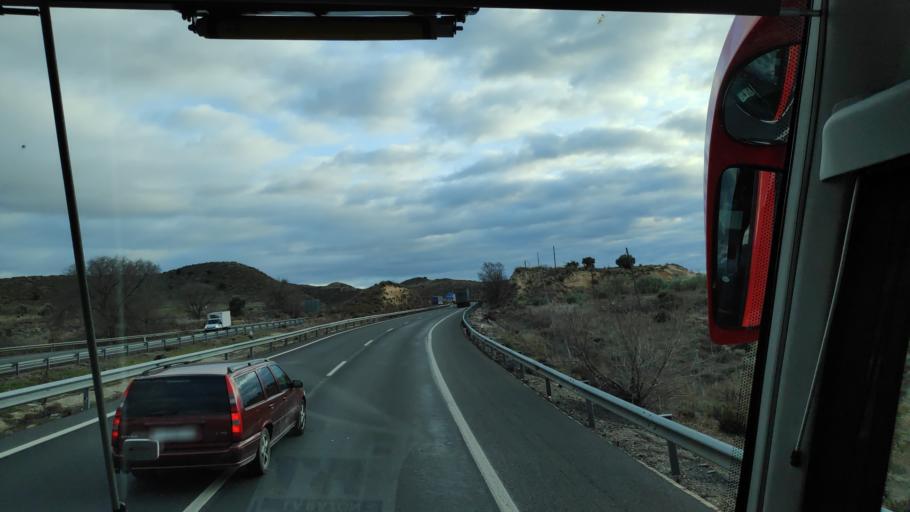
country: ES
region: Madrid
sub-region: Provincia de Madrid
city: Perales de Tajuna
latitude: 40.2194
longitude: -3.3299
